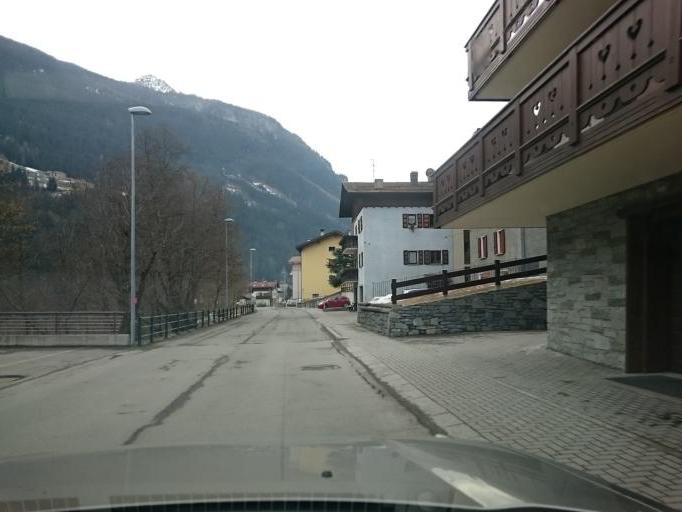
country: IT
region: Lombardy
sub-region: Provincia di Sondrio
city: Cepina
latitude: 46.4377
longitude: 10.3567
